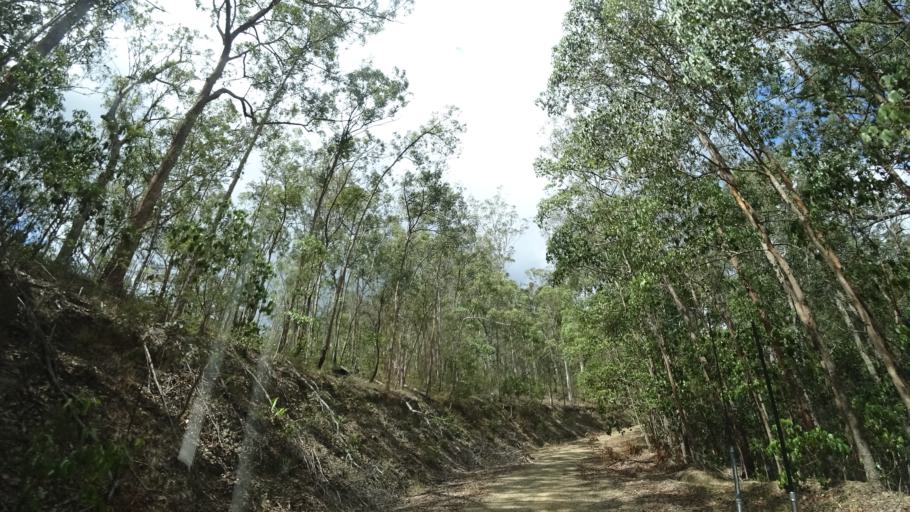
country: AU
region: Queensland
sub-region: Moreton Bay
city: Highvale
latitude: -27.3544
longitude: 152.7259
